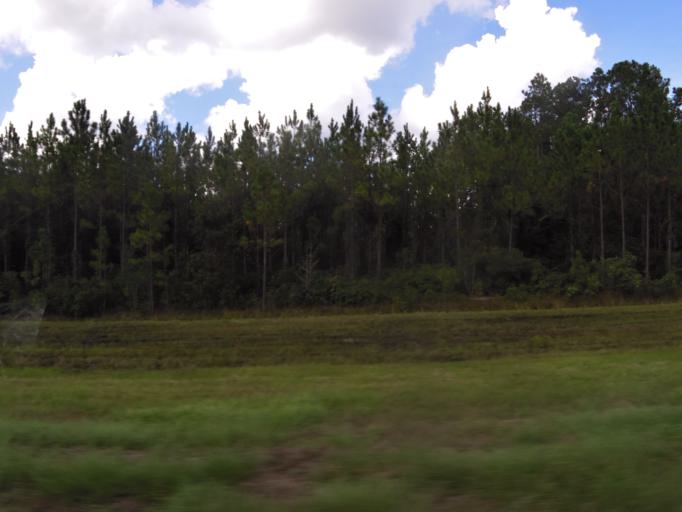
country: US
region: Florida
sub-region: Hamilton County
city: Jasper
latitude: 30.6714
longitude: -82.7576
